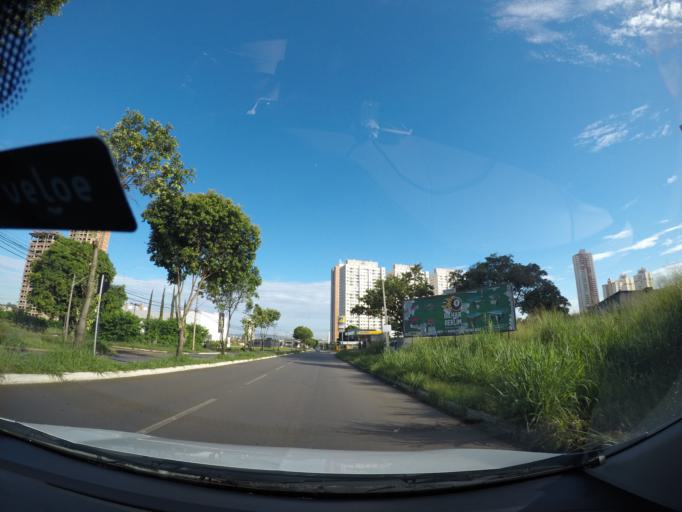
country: BR
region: Goias
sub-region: Goiania
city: Goiania
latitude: -16.7381
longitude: -49.2856
